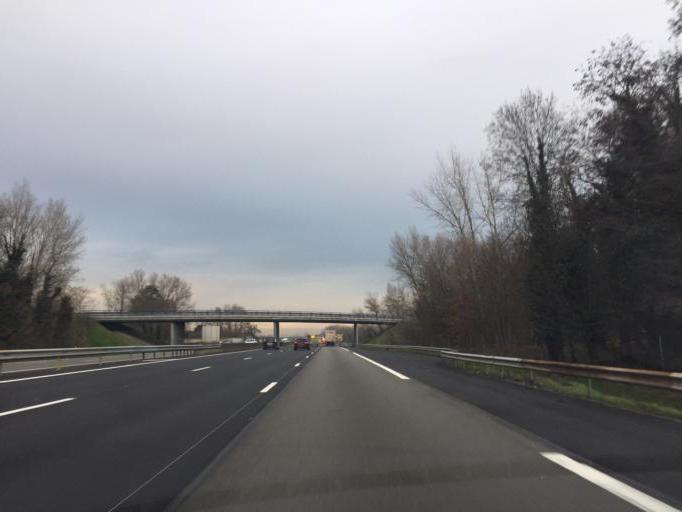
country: FR
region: Rhone-Alpes
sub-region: Departement du Rhone
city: Saint-Georges-de-Reneins
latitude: 46.0710
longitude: 4.7410
